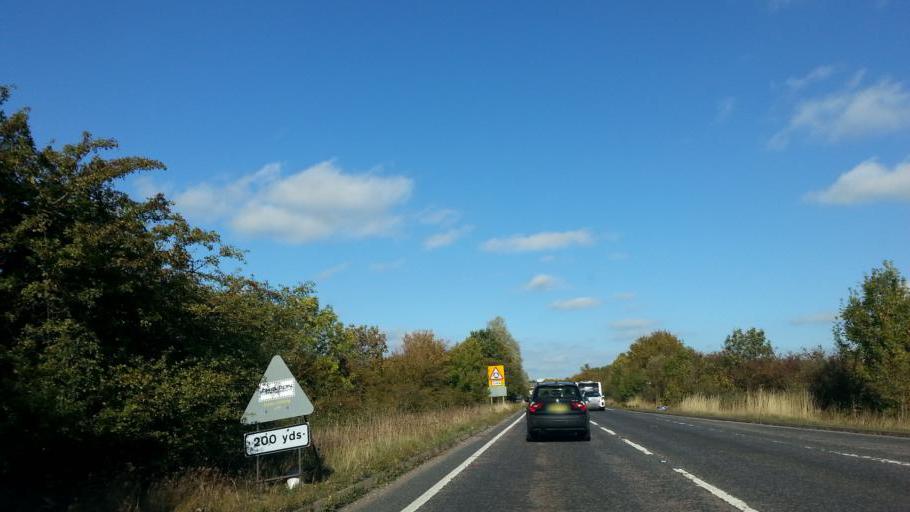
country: GB
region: England
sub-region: Northamptonshire
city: Thrapston
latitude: 52.3839
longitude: -0.5238
